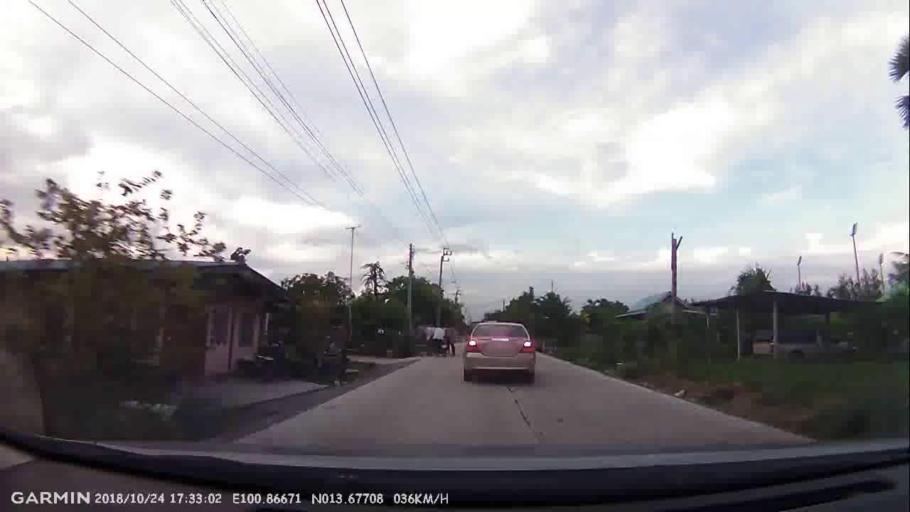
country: TH
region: Samut Prakan
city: Ban Khlong Bang Sao Thong
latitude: 13.6772
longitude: 100.8667
